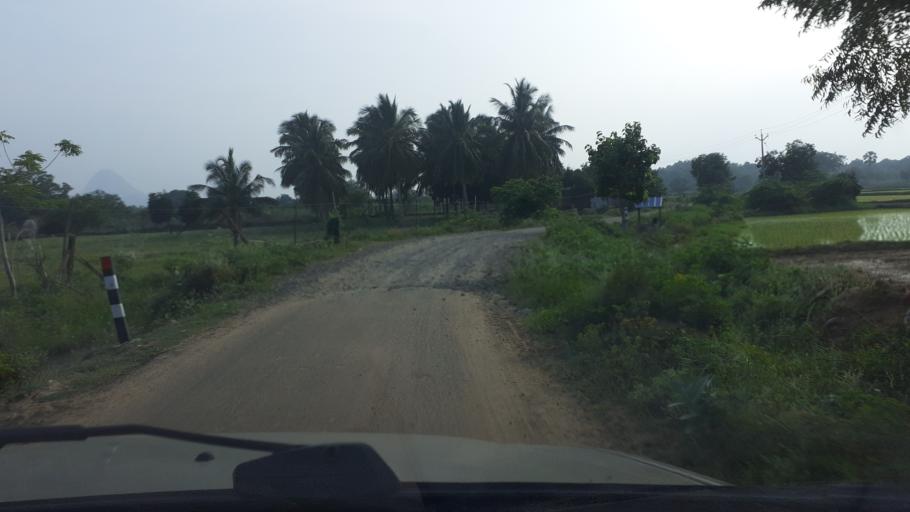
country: IN
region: Tamil Nadu
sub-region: Tirunelveli Kattabo
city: Kalakkadu
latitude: 8.4708
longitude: 77.5857
